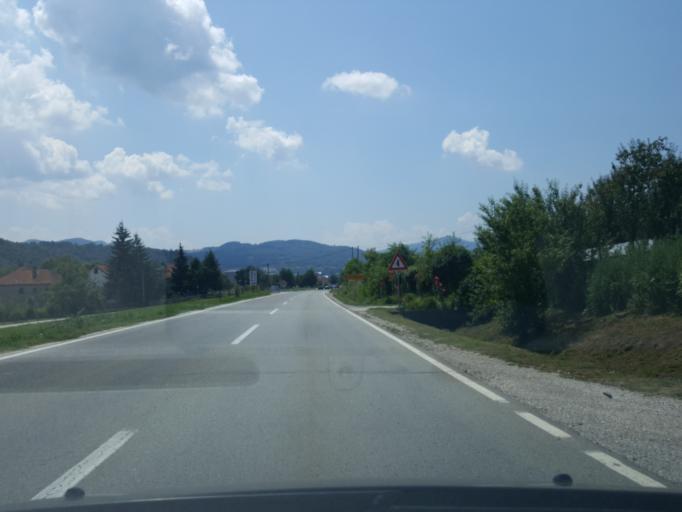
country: RS
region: Central Serbia
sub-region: Moravicki Okrug
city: Gornji Milanovac
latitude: 44.0643
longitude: 20.4911
